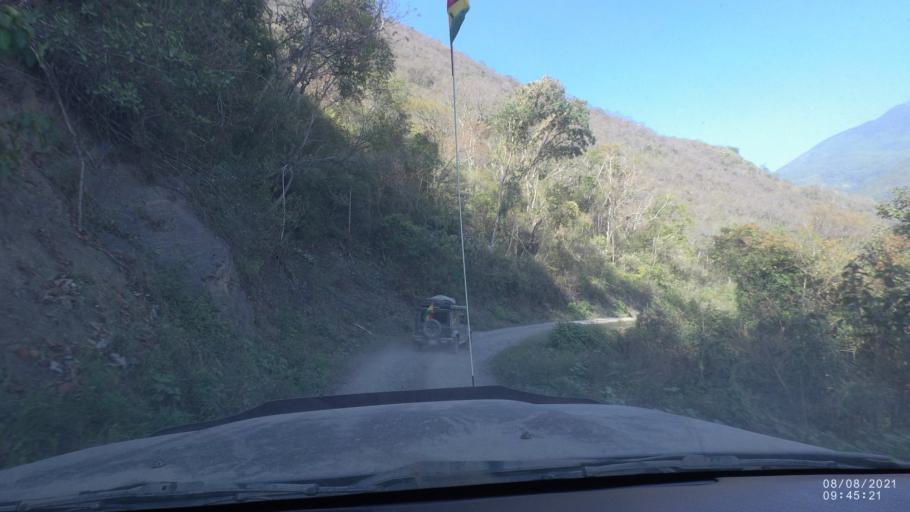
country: BO
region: La Paz
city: Quime
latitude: -16.6037
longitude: -66.7262
